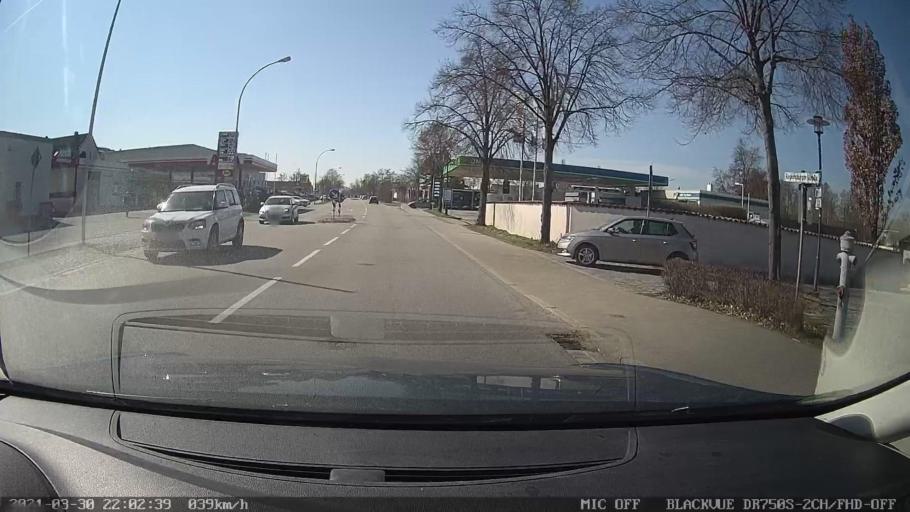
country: DE
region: Bavaria
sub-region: Upper Palatinate
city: Regenstauf
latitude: 49.1197
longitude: 12.1264
